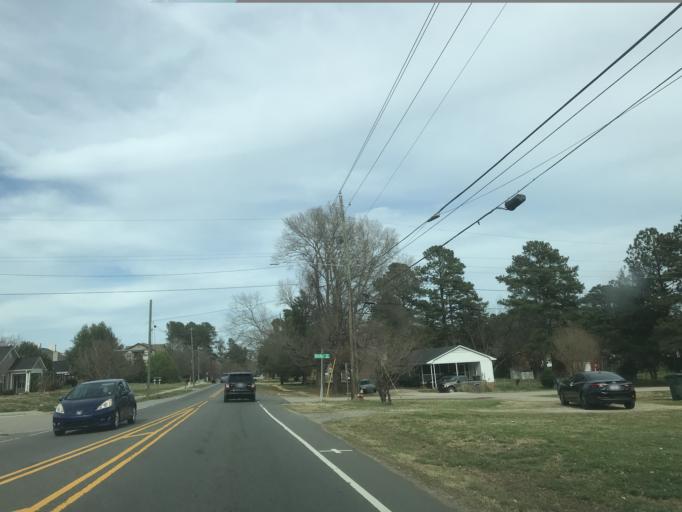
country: US
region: North Carolina
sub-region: Wake County
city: West Raleigh
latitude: 35.7445
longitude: -78.6784
